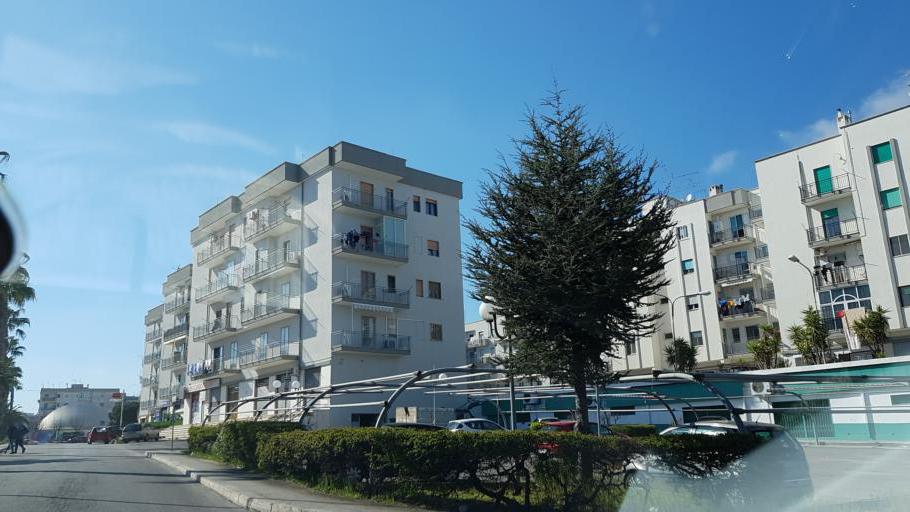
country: IT
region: Apulia
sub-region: Provincia di Brindisi
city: Ostuni
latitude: 40.7232
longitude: 17.5834
